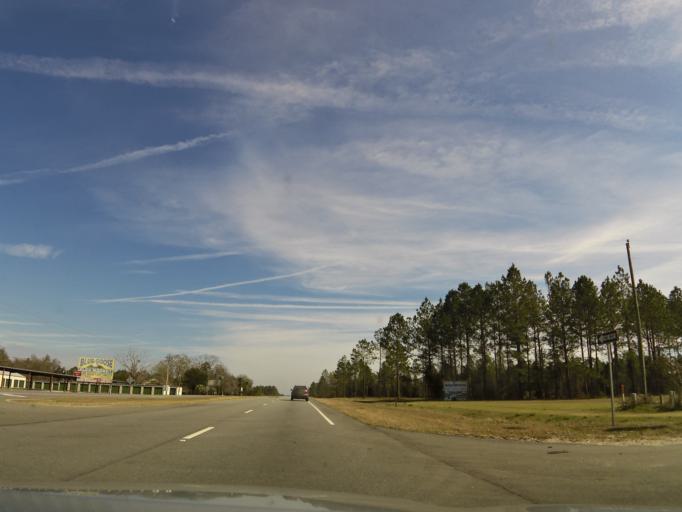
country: US
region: Georgia
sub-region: Brantley County
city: Nahunta
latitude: 31.2159
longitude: -81.8922
